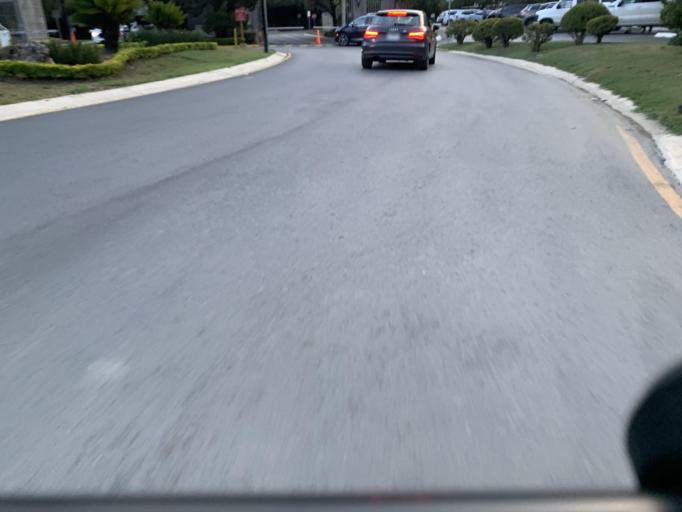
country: MX
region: Nuevo Leon
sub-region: Juarez
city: Bosques de San Pedro
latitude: 25.5169
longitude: -100.1977
